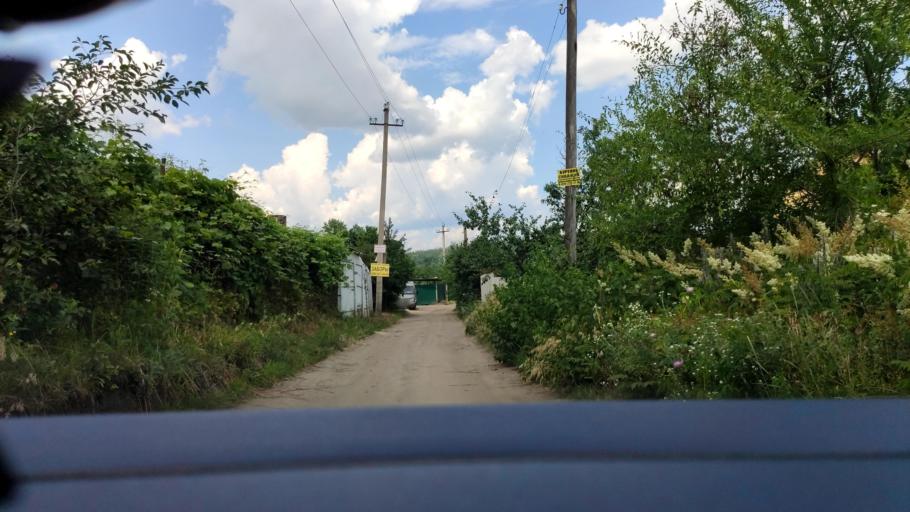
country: RU
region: Voronezj
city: Maslovka
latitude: 51.6068
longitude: 39.2863
